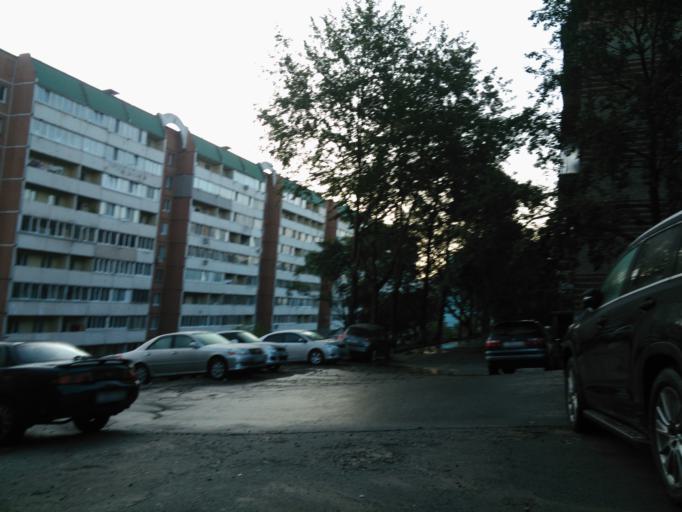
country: RU
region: Primorskiy
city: Vladivostok
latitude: 43.0935
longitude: 131.9626
